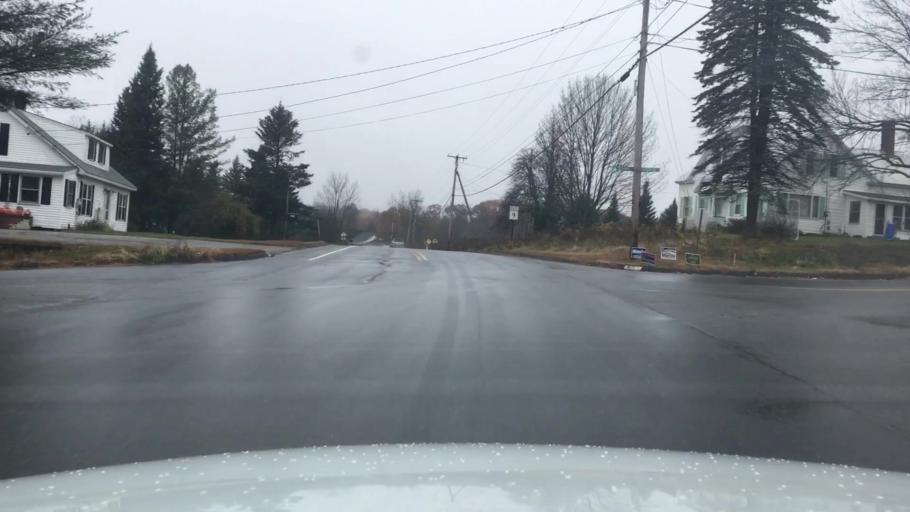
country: US
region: Maine
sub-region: Androscoggin County
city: Sabattus
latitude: 44.1108
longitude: -70.0906
